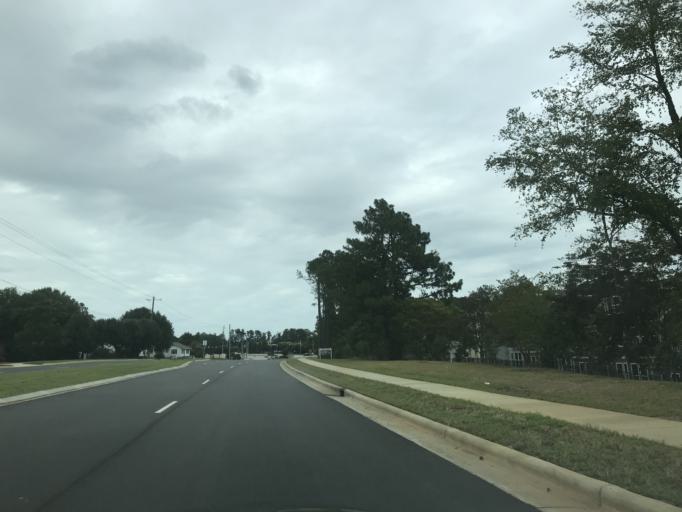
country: US
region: North Carolina
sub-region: Wake County
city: Cary
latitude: 35.7412
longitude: -78.7423
